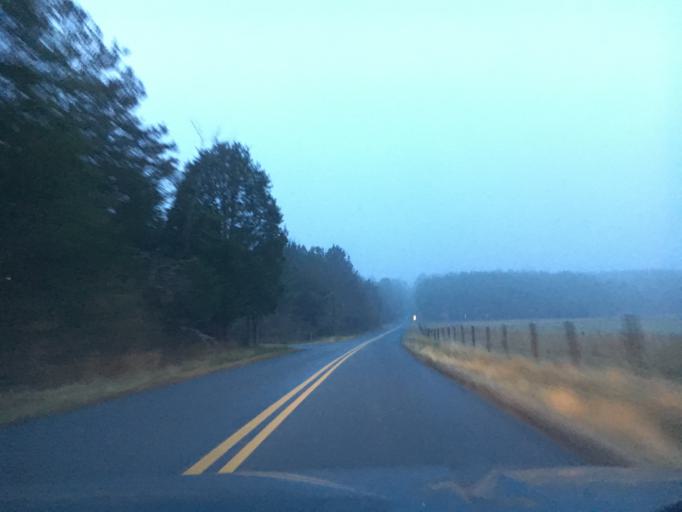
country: US
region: Virginia
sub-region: Halifax County
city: Mountain Road
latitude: 36.6819
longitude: -79.0306
